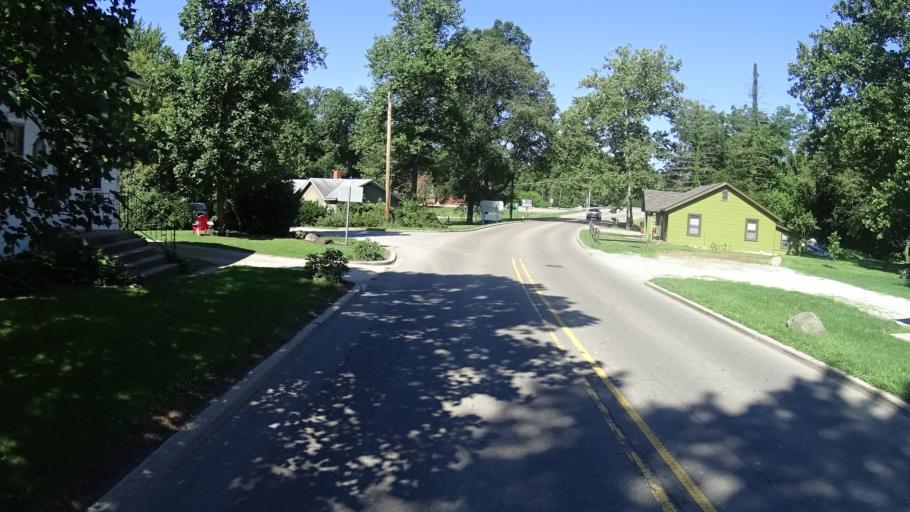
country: US
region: Indiana
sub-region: Madison County
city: Pendleton
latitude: 40.0023
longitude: -85.7530
